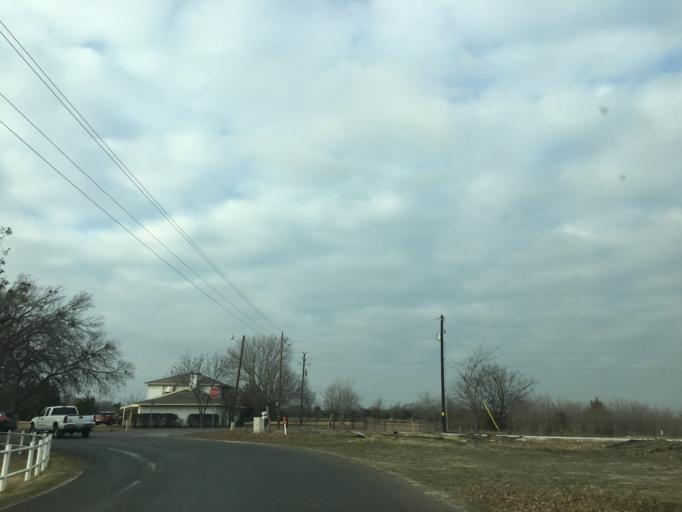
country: US
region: Texas
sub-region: Ellis County
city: Red Oak
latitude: 32.4844
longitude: -96.7906
